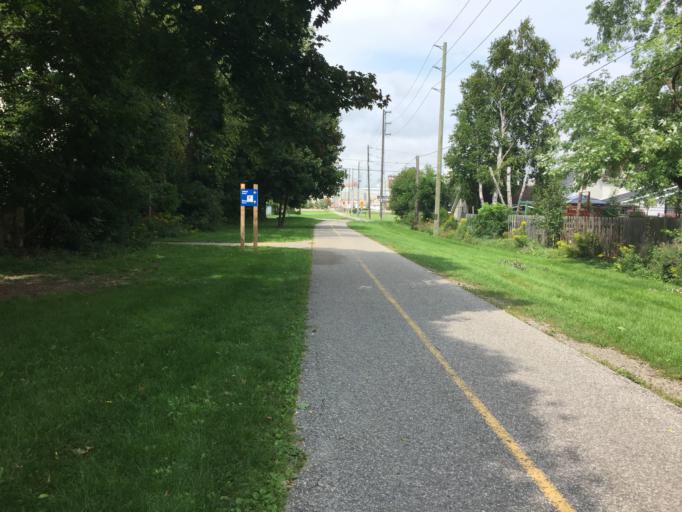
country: CA
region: Ontario
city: Oshawa
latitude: 43.8926
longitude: -78.8579
